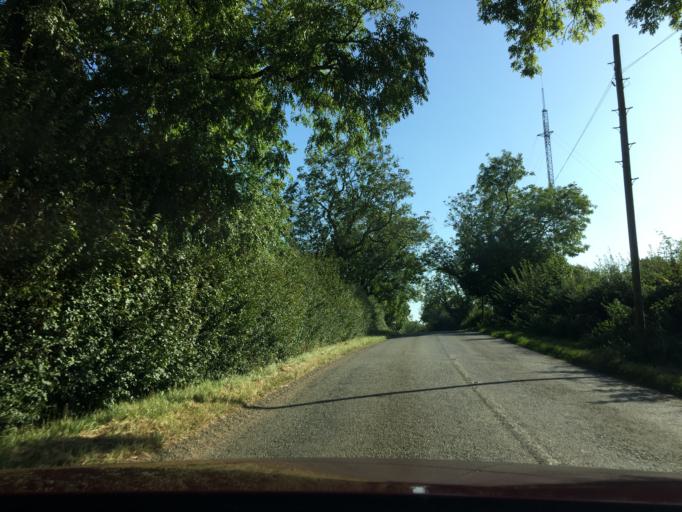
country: GB
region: England
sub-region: Leicestershire
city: Houghton on the Hill
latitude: 52.6385
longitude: -0.9330
